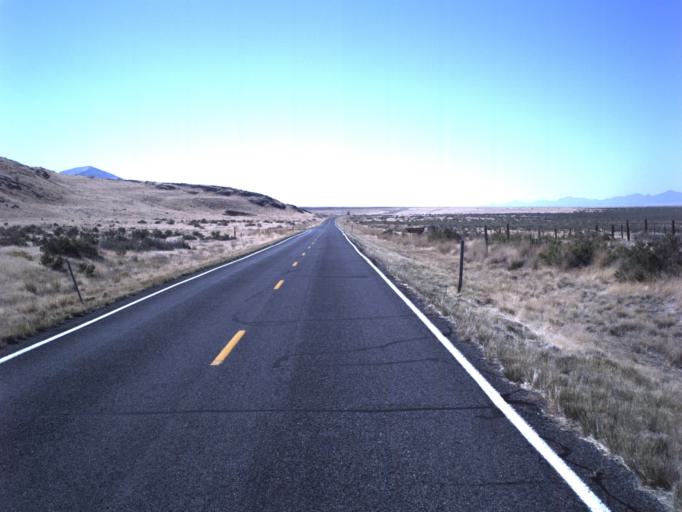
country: US
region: Utah
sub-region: Tooele County
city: Grantsville
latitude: 40.6172
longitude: -112.7024
